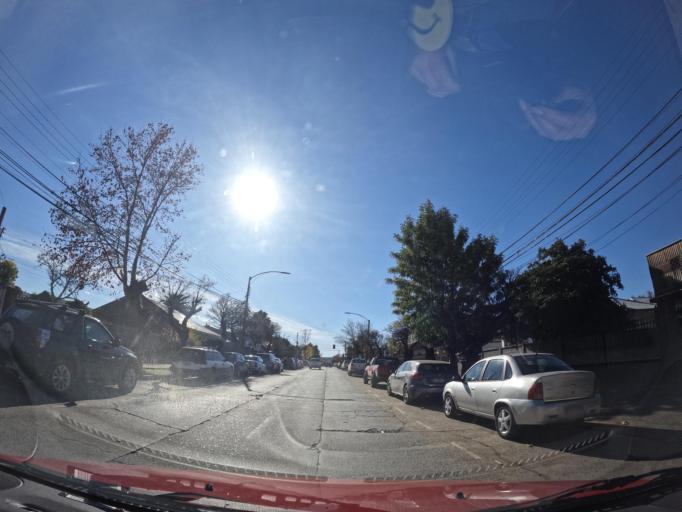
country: CL
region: Maule
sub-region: Provincia de Cauquenes
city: Cauquenes
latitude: -35.9650
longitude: -72.3146
